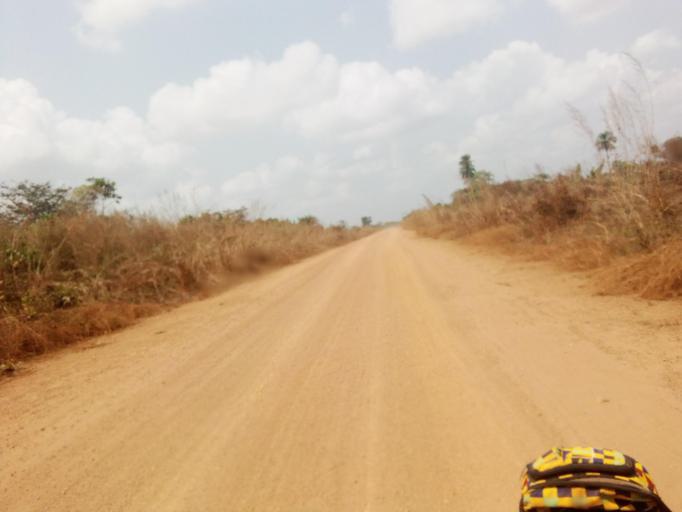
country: SL
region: Southern Province
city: Mogbwemo
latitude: 7.6616
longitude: -12.2686
